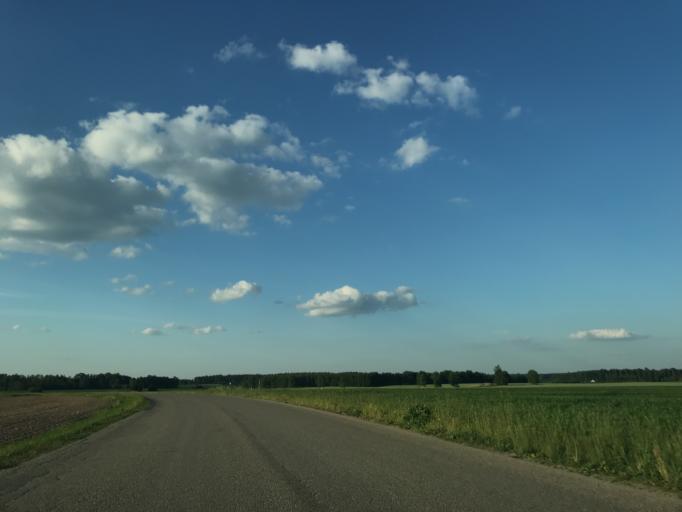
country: LV
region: Lecava
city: Iecava
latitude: 56.6093
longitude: 24.2435
